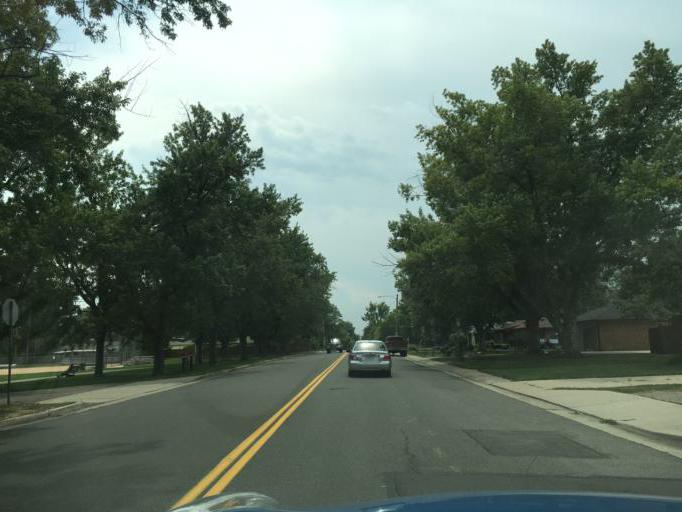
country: US
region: Colorado
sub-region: Jefferson County
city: Wheat Ridge
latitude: 39.7469
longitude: -105.0908
